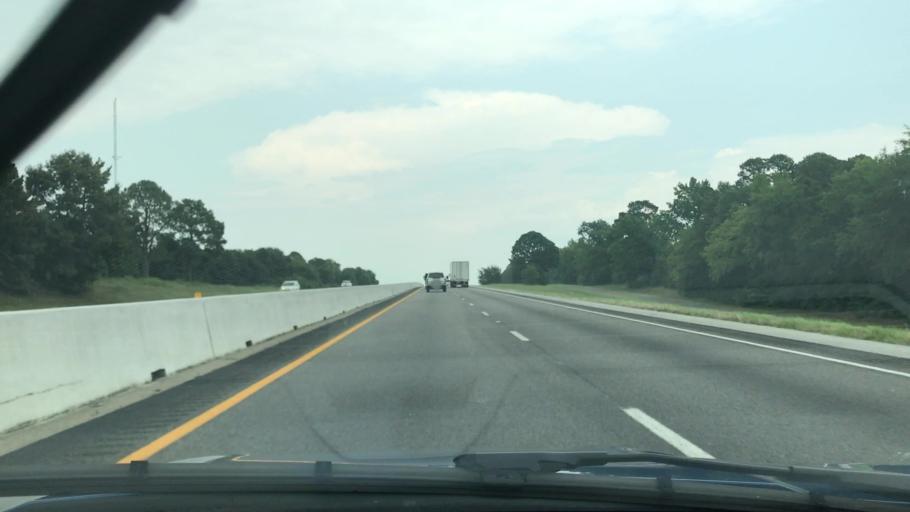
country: US
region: Texas
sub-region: Gregg County
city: Liberty City
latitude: 32.4376
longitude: -95.0259
